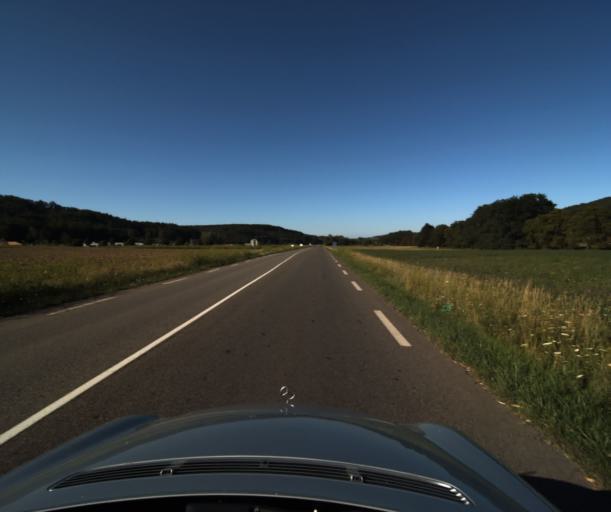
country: FR
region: Midi-Pyrenees
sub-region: Departement de l'Ariege
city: Lavelanet
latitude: 42.9989
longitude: 1.8805
